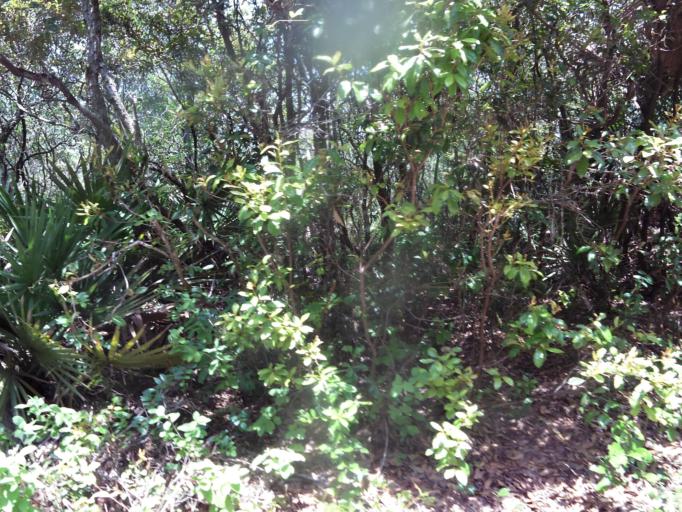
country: US
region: Florida
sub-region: Nassau County
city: Fernandina Beach
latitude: 30.4983
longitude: -81.4934
